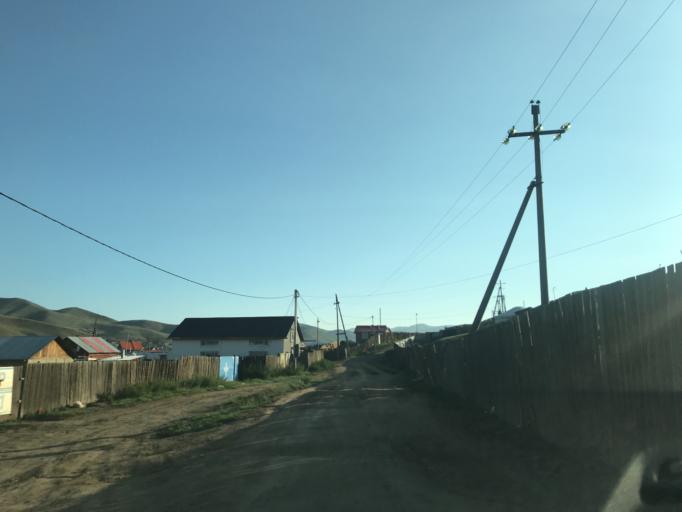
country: MN
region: Ulaanbaatar
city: Ulaanbaatar
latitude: 47.9897
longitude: 106.9644
